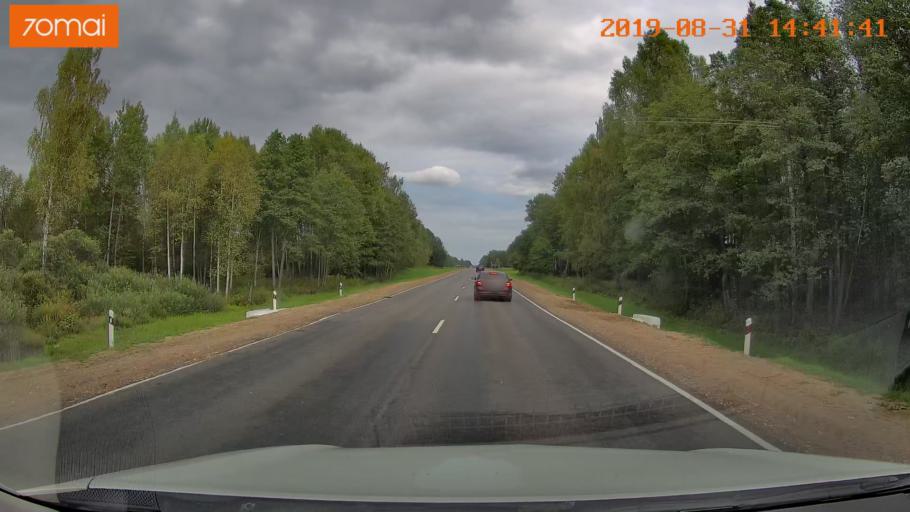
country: RU
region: Smolensk
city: Yekimovichi
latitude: 54.2042
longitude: 33.5951
